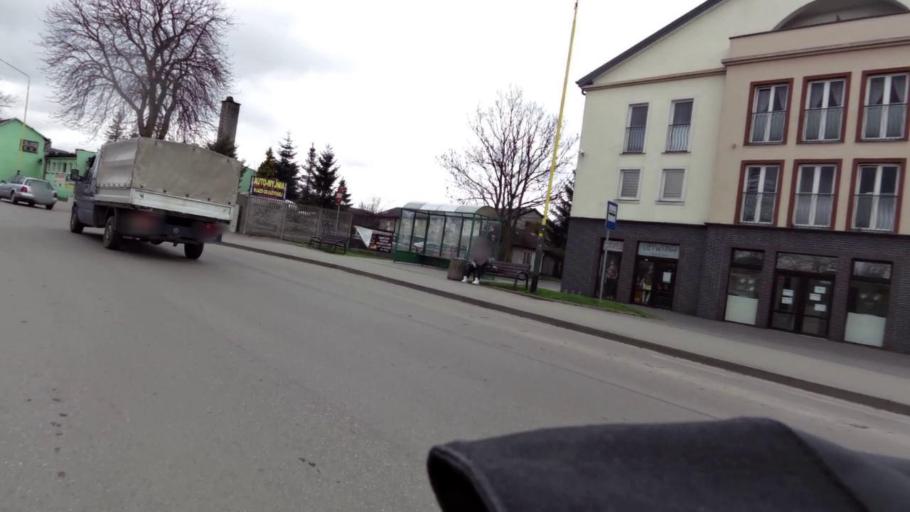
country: PL
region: West Pomeranian Voivodeship
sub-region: Powiat koszalinski
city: Sianow
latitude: 54.2279
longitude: 16.2962
